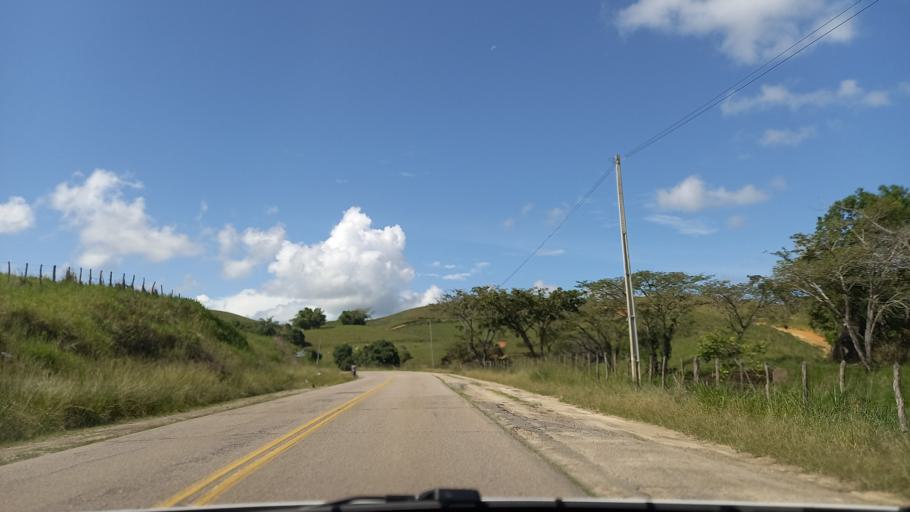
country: BR
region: Pernambuco
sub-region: Barreiros
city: Barreiros
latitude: -8.7568
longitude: -35.1720
